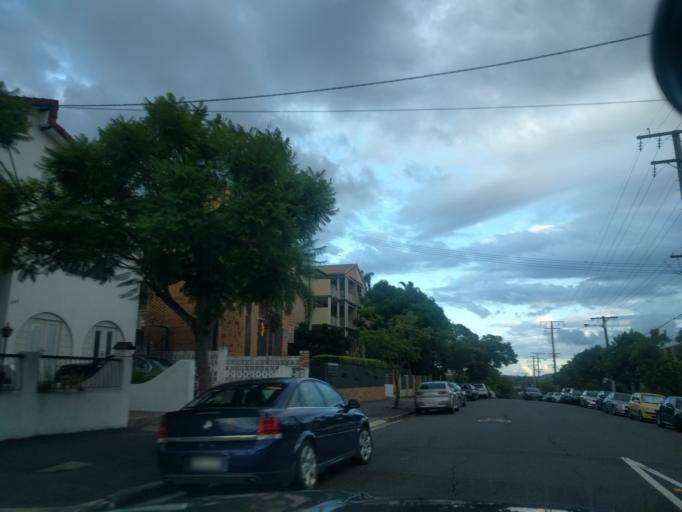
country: AU
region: Queensland
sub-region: Brisbane
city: Fortitude Valley
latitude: -27.4656
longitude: 153.0420
